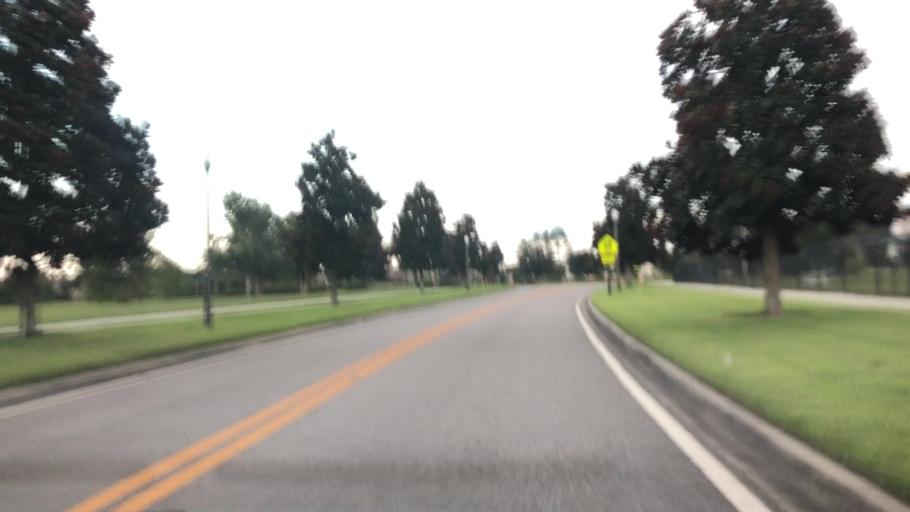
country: US
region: Florida
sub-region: Saint Johns County
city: Palm Valley
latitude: 30.1003
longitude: -81.4560
